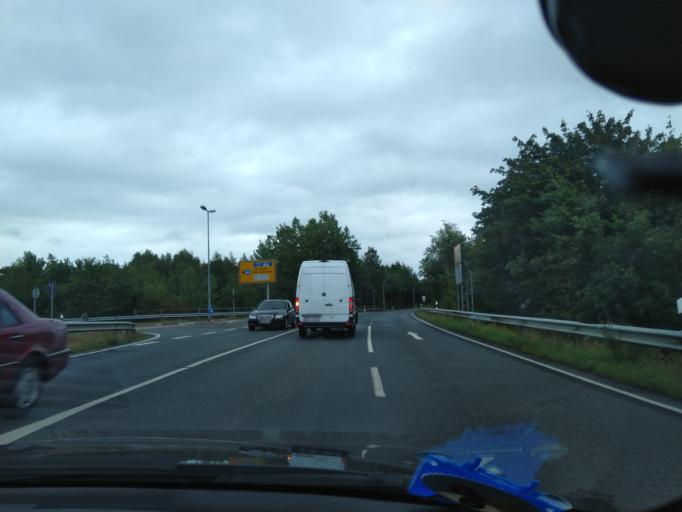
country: DE
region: Lower Saxony
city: Nordhorn
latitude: 52.4210
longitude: 7.0881
